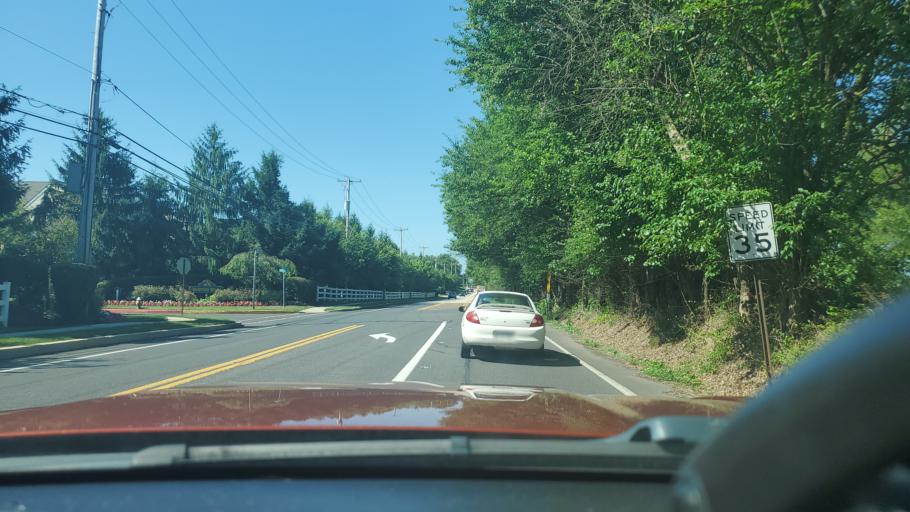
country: US
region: Pennsylvania
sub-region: Montgomery County
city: Limerick
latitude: 40.2273
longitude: -75.5350
